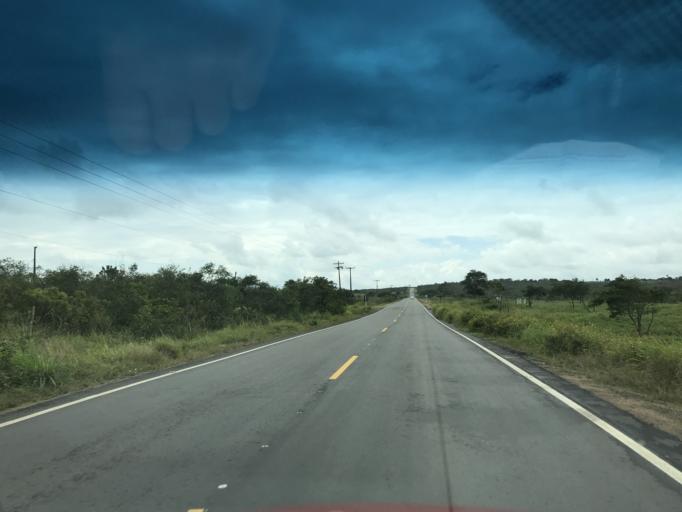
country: BR
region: Bahia
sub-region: Castro Alves
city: Castro Alves
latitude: -12.6739
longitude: -39.2941
